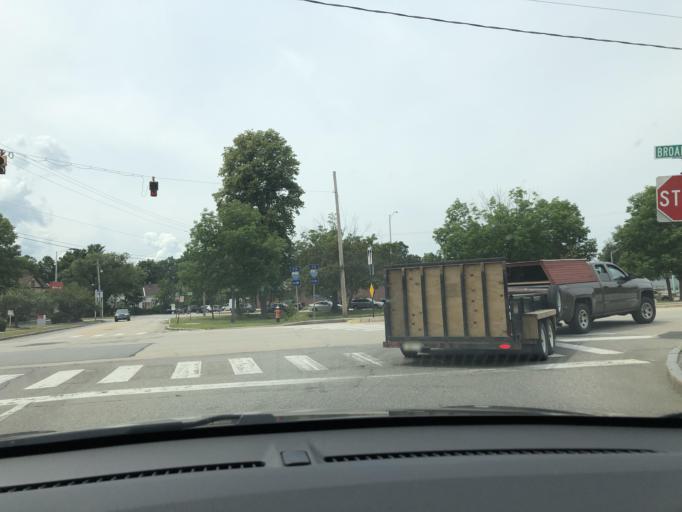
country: US
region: New Hampshire
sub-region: Merrimack County
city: Concord
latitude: 43.1938
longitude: -71.5386
